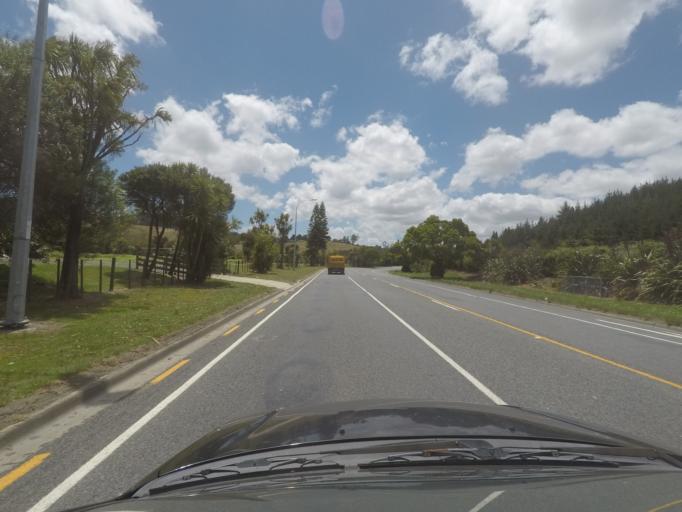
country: NZ
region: Northland
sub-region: Whangarei
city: Whangarei
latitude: -35.7497
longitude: 174.3204
